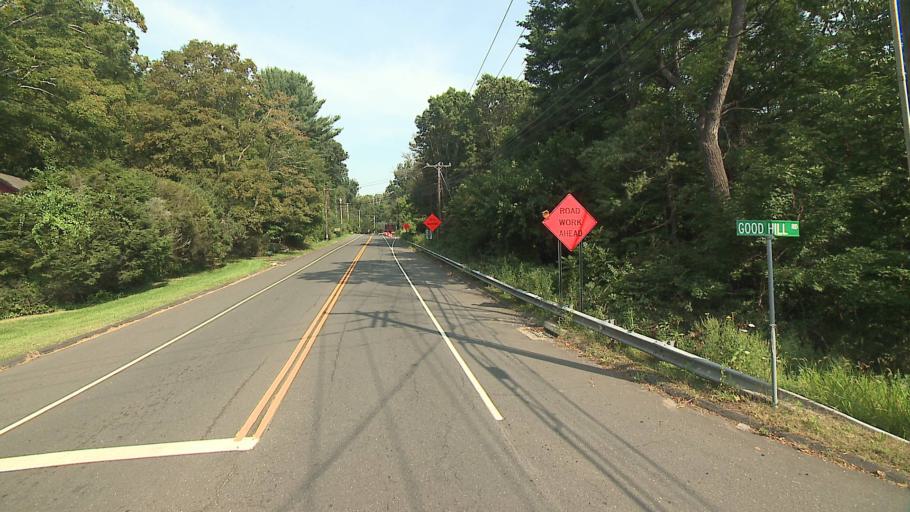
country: US
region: Connecticut
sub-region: Fairfield County
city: Westport
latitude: 41.1848
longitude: -73.3690
